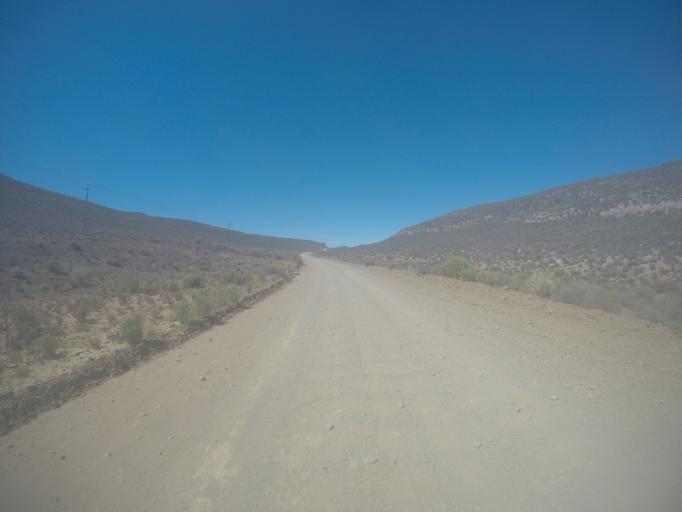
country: ZA
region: Western Cape
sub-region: West Coast District Municipality
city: Clanwilliam
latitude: -32.5238
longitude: 19.3513
